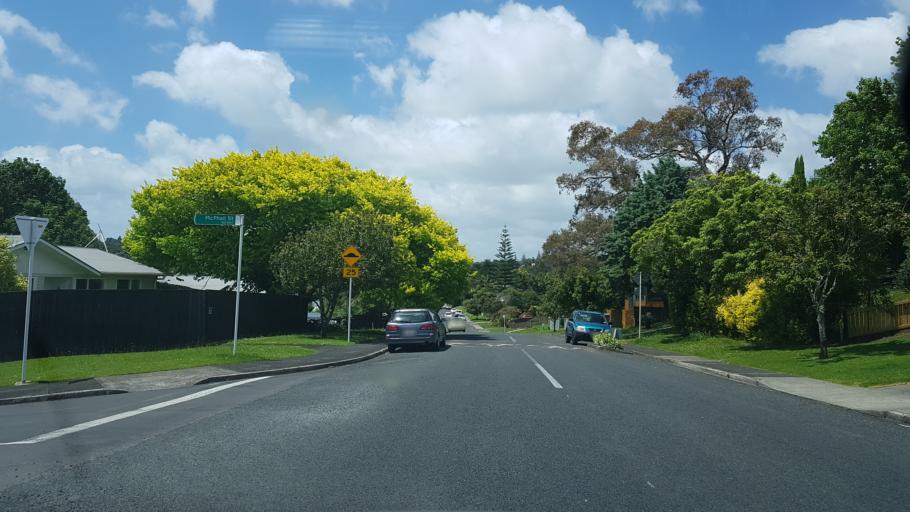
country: NZ
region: Auckland
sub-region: Auckland
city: North Shore
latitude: -36.7891
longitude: 174.7027
